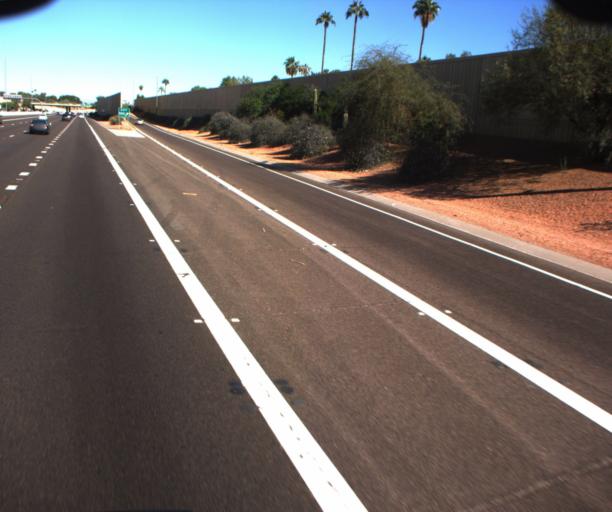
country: US
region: Arizona
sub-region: Maricopa County
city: Tempe
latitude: 33.3726
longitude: -111.8933
